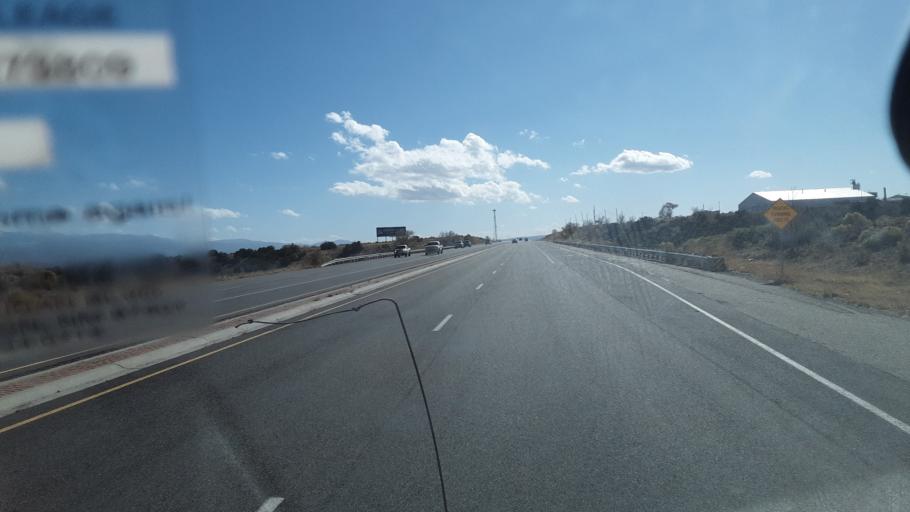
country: US
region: New Mexico
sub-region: Rio Arriba County
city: Ohkay Owingeh
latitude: 36.0248
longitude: -106.0922
